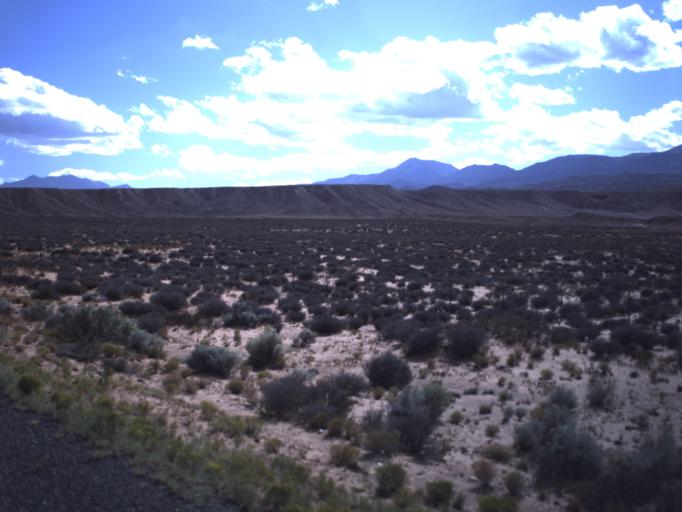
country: US
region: Utah
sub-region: Wayne County
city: Loa
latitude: 38.1577
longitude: -110.6215
